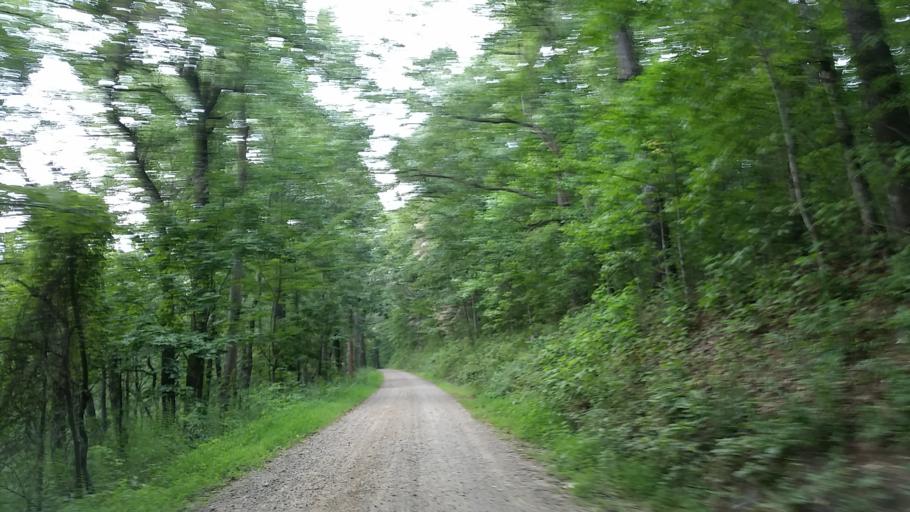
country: US
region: Georgia
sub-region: Lumpkin County
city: Dahlonega
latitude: 34.6465
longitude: -84.0611
